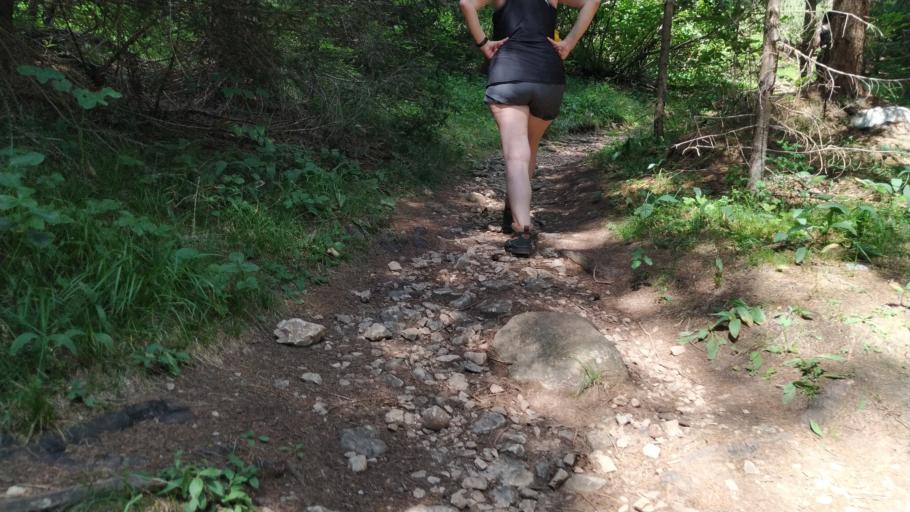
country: IT
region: Trentino-Alto Adige
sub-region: Bolzano
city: San Felice
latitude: 46.4863
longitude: 11.1541
